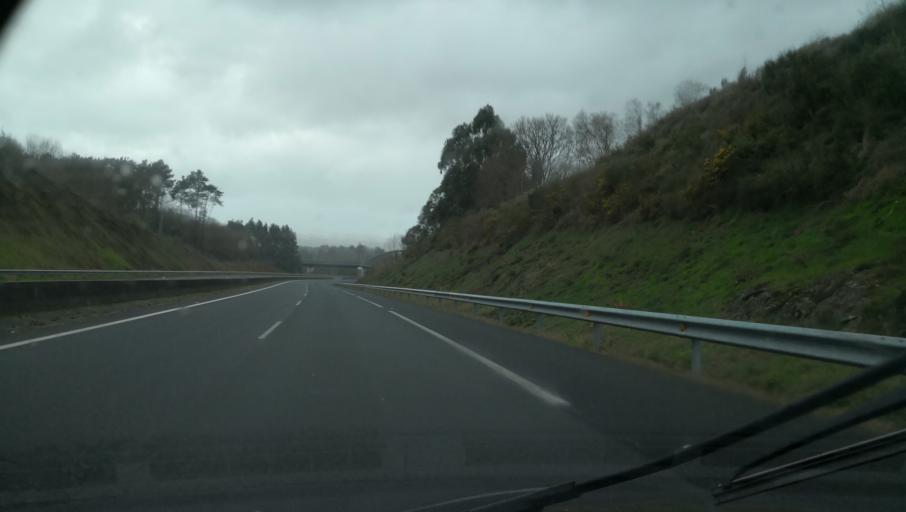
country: ES
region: Galicia
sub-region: Provincia de Pontevedra
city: Lalin
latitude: 42.6881
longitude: -8.1705
